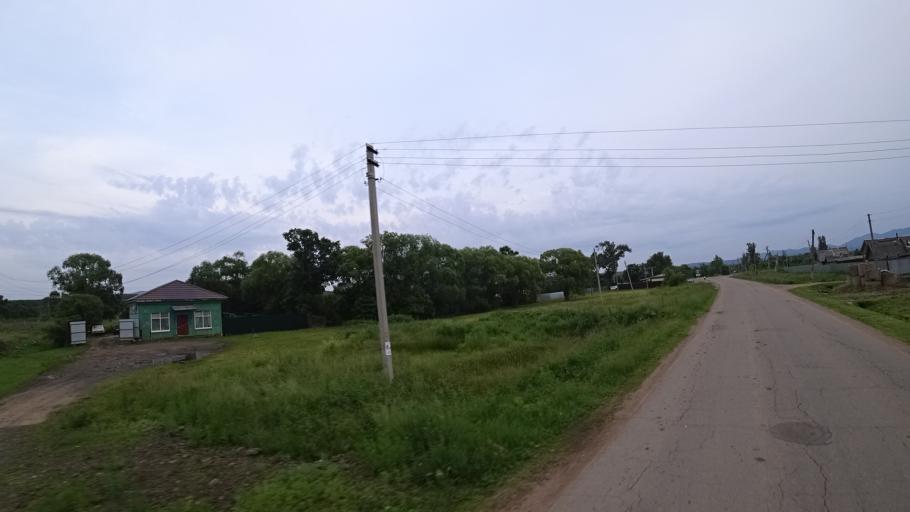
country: RU
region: Primorskiy
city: Novosysoyevka
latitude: 44.2329
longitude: 133.3709
